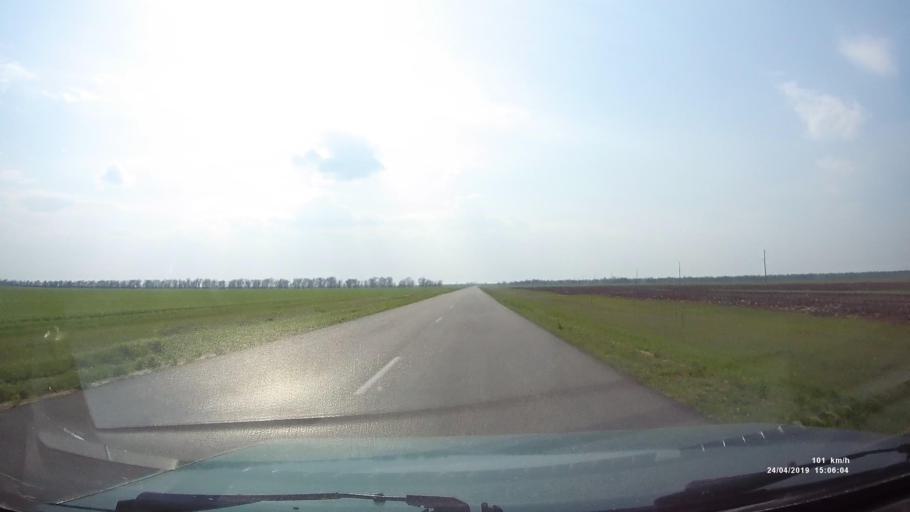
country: RU
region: Rostov
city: Remontnoye
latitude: 46.5593
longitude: 43.4354
